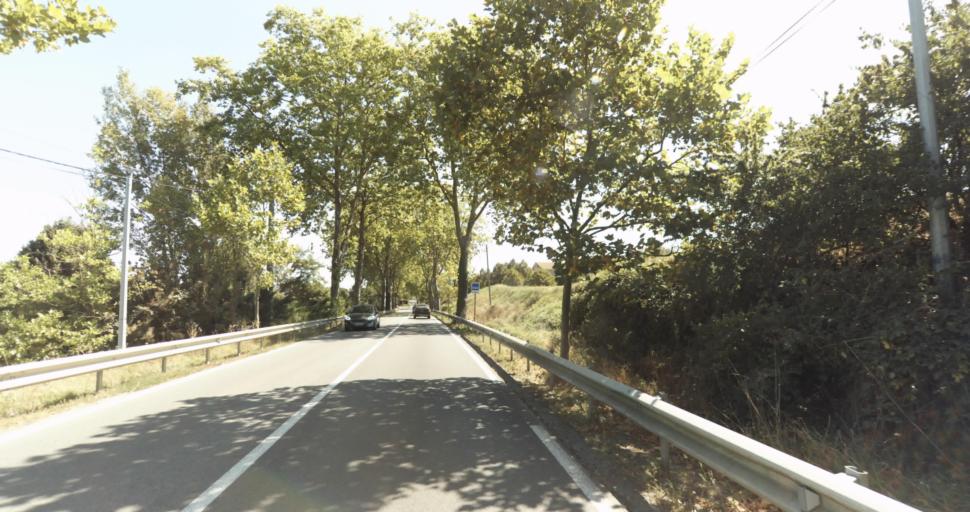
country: FR
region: Midi-Pyrenees
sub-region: Departement de la Haute-Garonne
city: Montrabe
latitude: 43.6444
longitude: 1.5112
